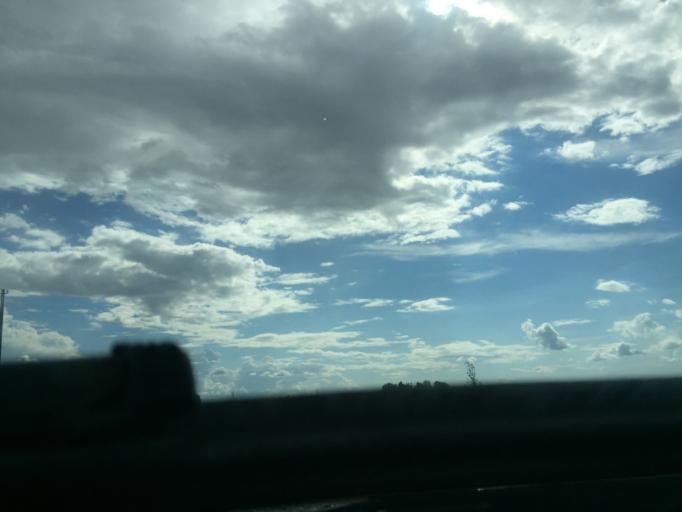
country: LT
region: Siauliu apskritis
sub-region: Joniskis
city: Joniskis
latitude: 56.3311
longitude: 23.5623
